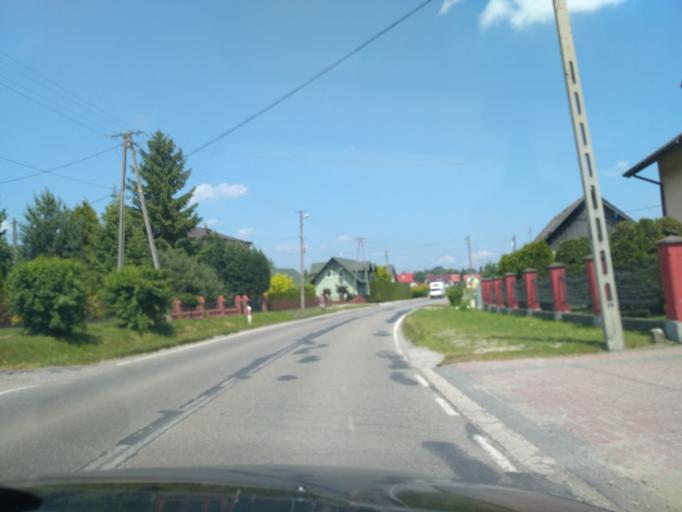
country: PL
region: Subcarpathian Voivodeship
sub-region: Powiat lancucki
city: Albigowa
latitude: 50.0213
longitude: 22.2242
